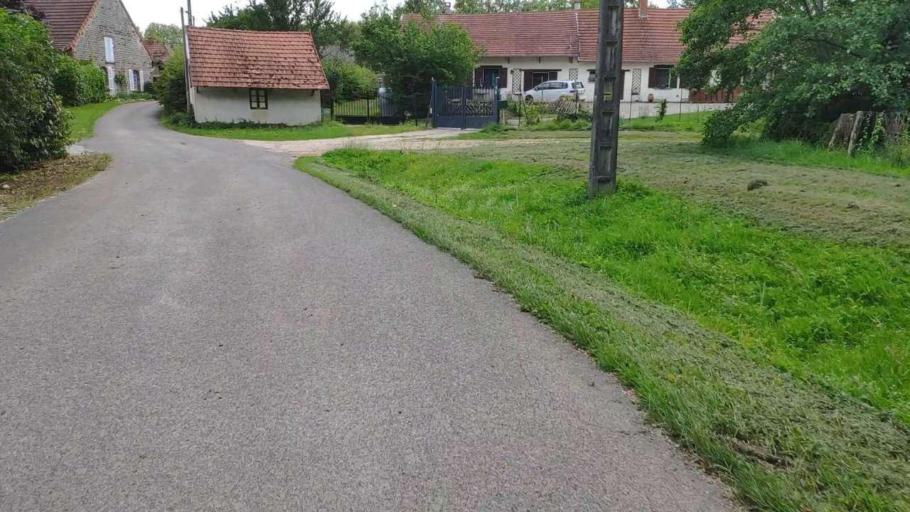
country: FR
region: Franche-Comte
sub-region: Departement du Jura
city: Bletterans
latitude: 46.8420
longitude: 5.4749
